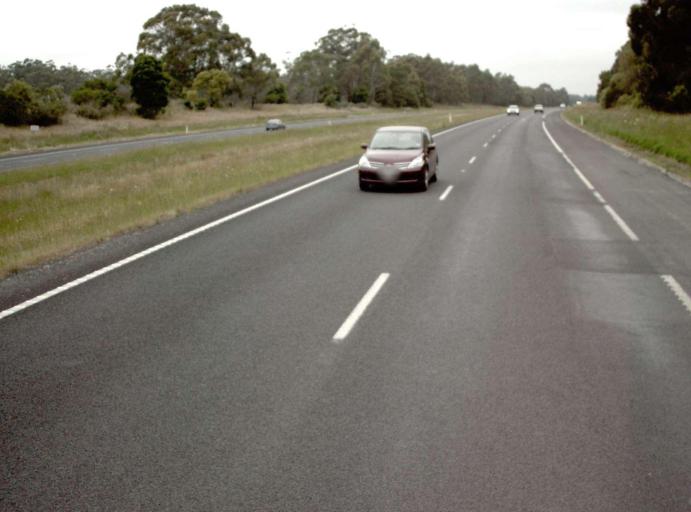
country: AU
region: Victoria
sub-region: Baw Baw
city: Warragul
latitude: -38.1041
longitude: 145.8550
